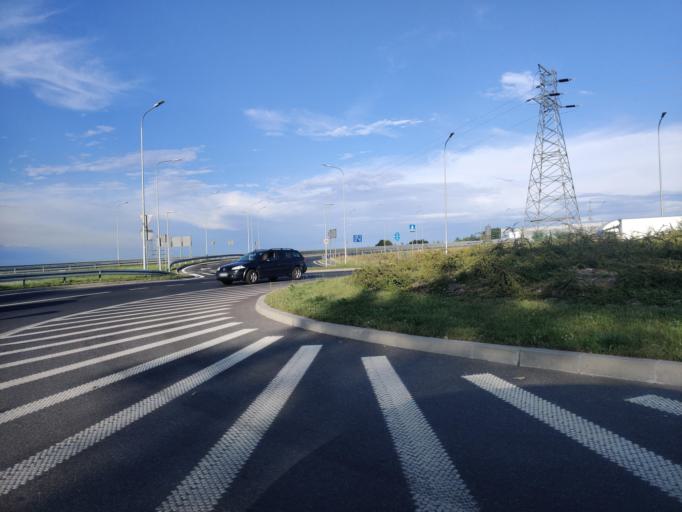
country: PL
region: Greater Poland Voivodeship
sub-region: Konin
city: Konin
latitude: 52.2038
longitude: 18.2704
